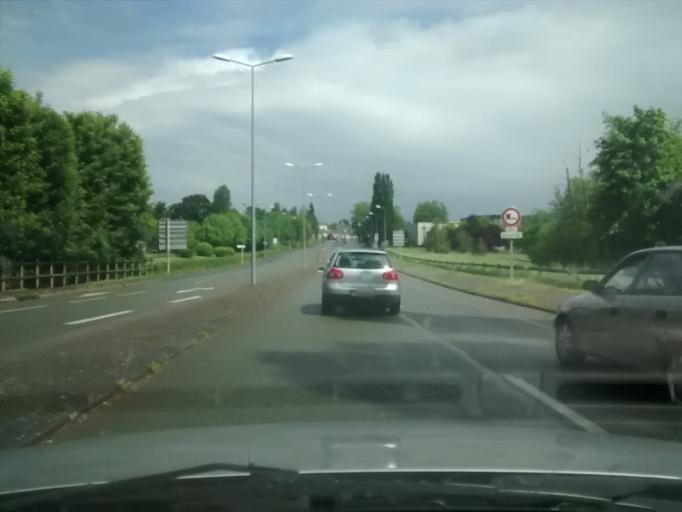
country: FR
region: Pays de la Loire
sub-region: Departement de la Mayenne
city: Laval
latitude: 48.0635
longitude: -0.7581
